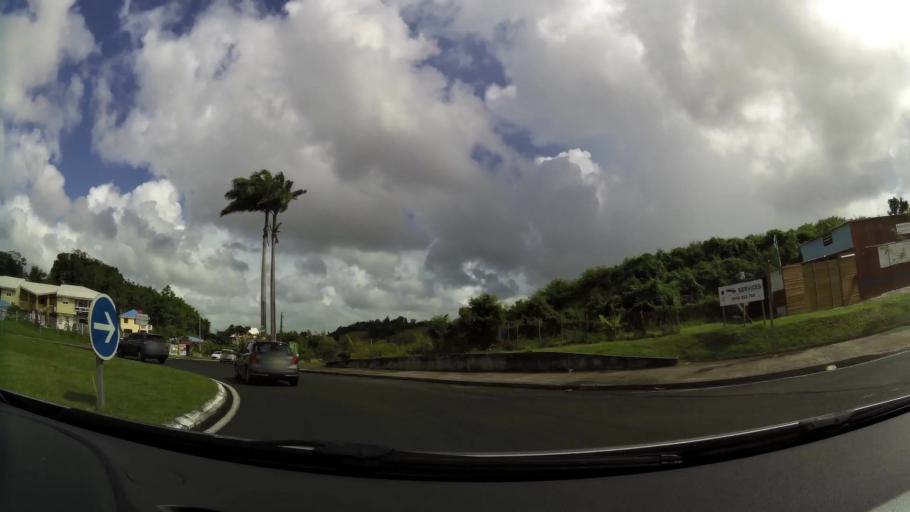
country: MQ
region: Martinique
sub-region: Martinique
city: Sainte-Luce
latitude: 14.5004
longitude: -60.9817
